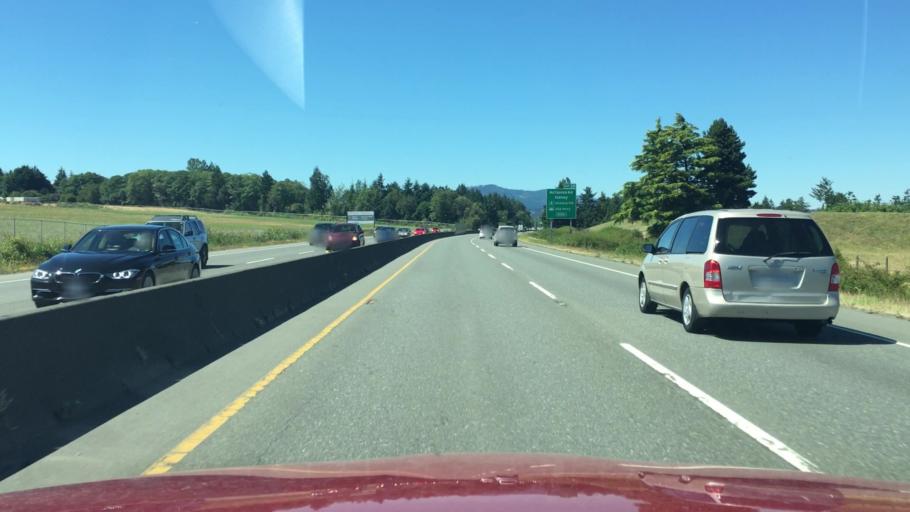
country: CA
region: British Columbia
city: North Saanich
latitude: 48.6199
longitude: -123.4071
